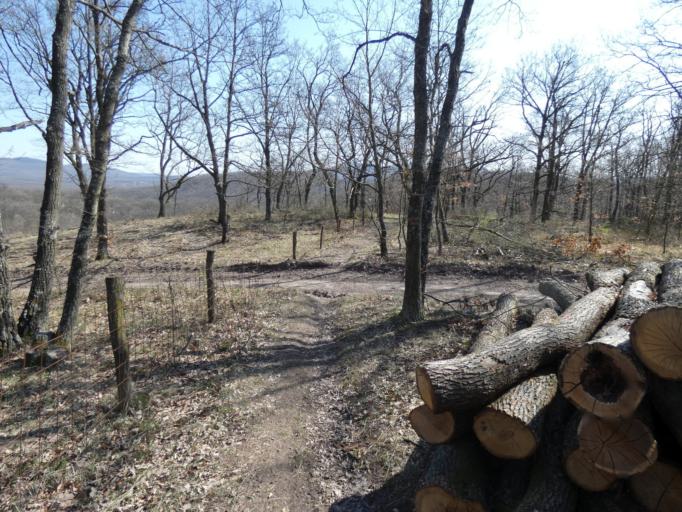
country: HU
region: Pest
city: Szob
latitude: 47.8686
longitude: 18.8977
